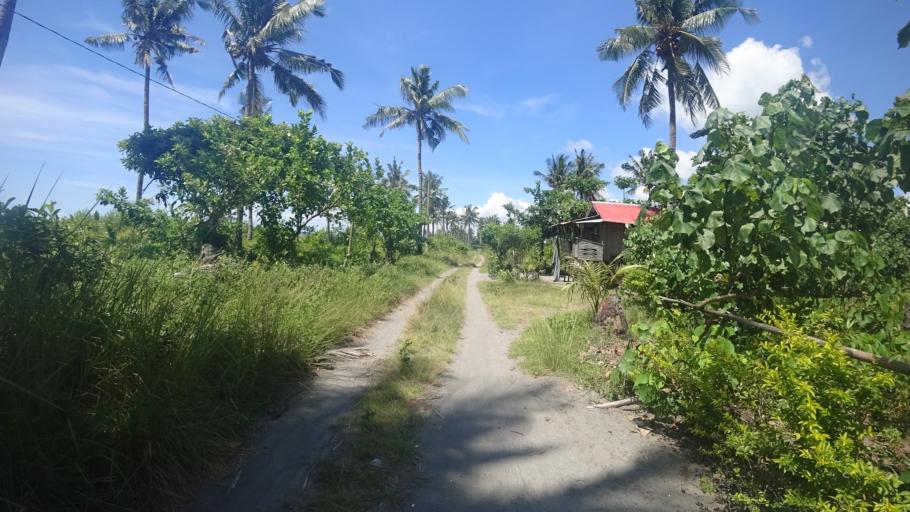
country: PH
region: Eastern Visayas
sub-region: Province of Leyte
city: Mayorga
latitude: 10.8922
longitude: 125.0139
